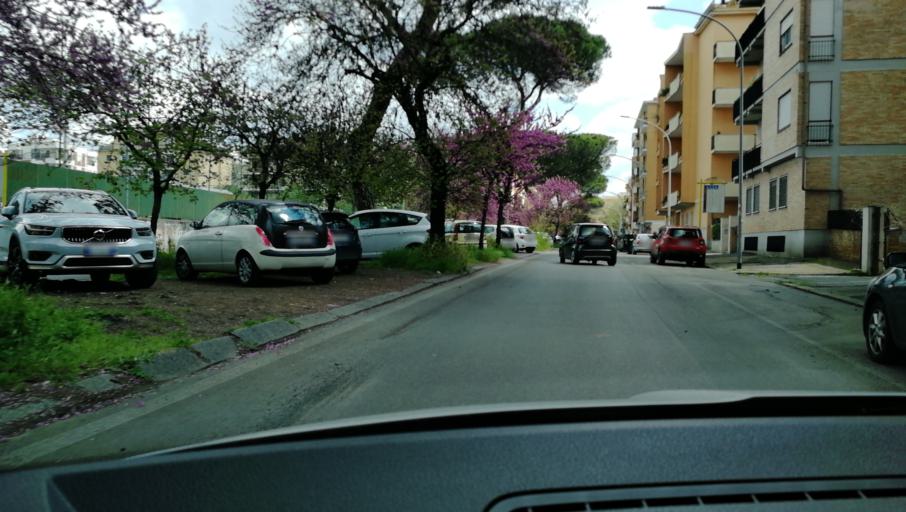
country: IT
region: Latium
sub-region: Citta metropolitana di Roma Capitale
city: Rome
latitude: 41.8518
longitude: 12.4993
